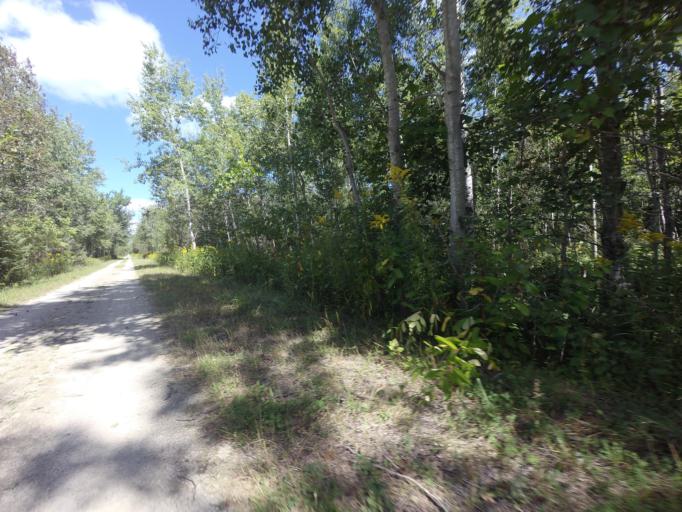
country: CA
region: Ontario
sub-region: Wellington County
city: Guelph
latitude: 43.7526
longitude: -80.3202
